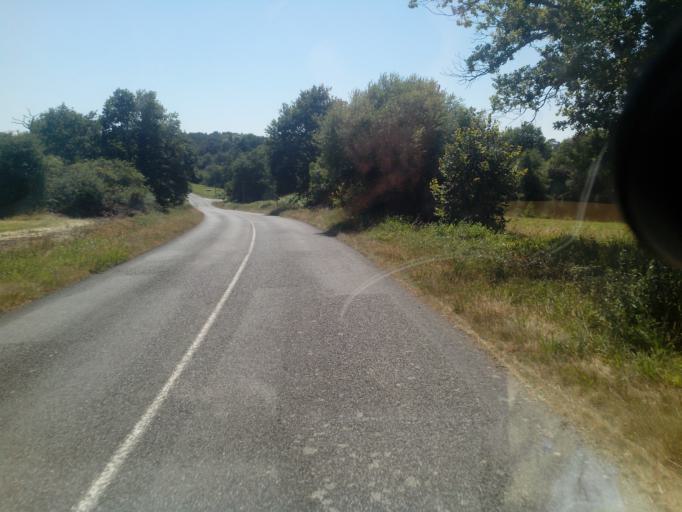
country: FR
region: Brittany
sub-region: Departement du Morbihan
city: Campeneac
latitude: 47.9985
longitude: -2.2484
